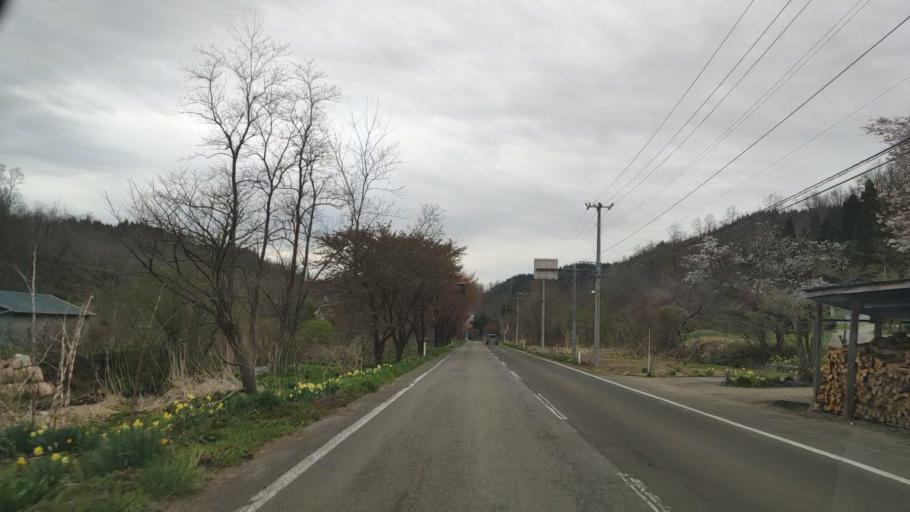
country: JP
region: Akita
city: Hanawa
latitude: 40.3555
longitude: 140.7811
